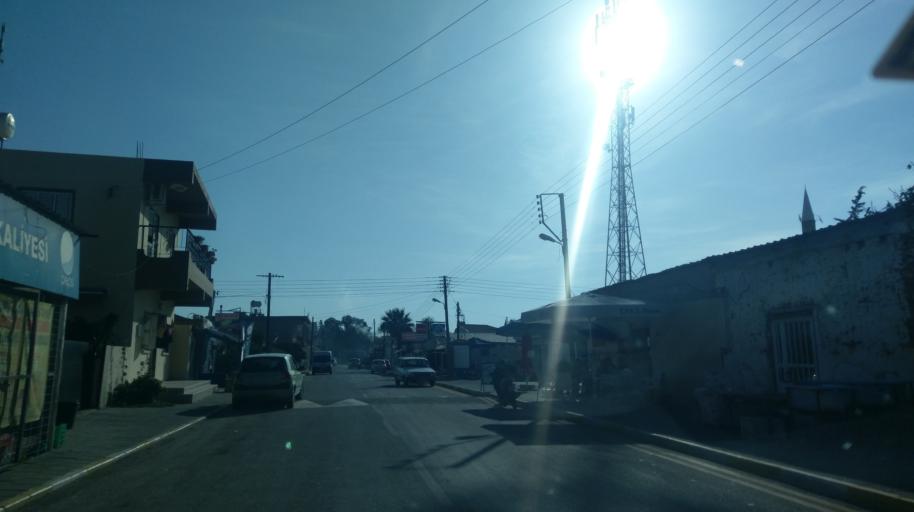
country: CY
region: Larnaka
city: Pergamos
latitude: 35.0410
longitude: 33.7076
